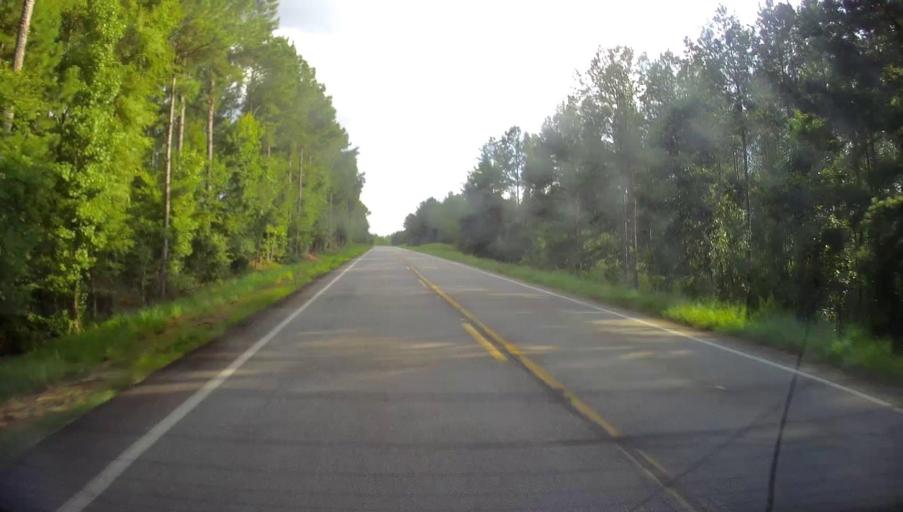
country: US
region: Georgia
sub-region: Crawford County
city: Roberta
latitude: 32.8210
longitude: -84.0217
